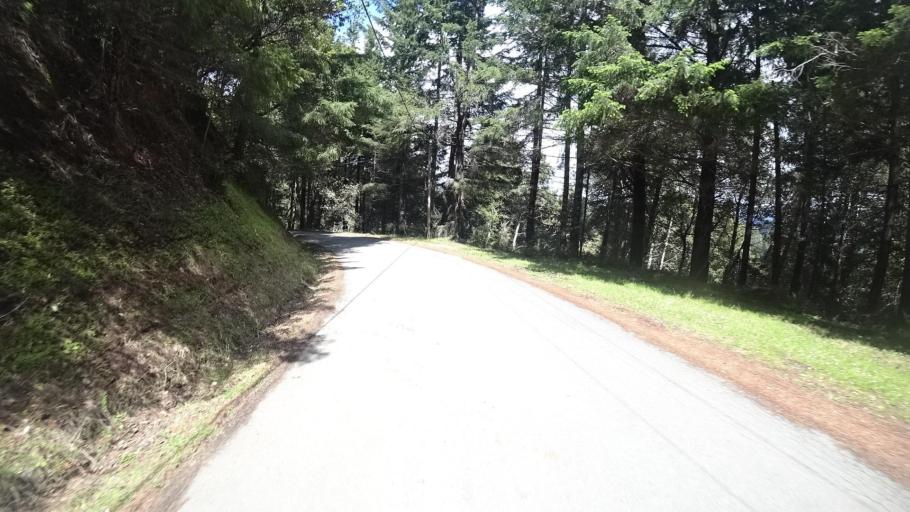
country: US
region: California
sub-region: Humboldt County
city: Blue Lake
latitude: 40.7632
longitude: -123.9459
